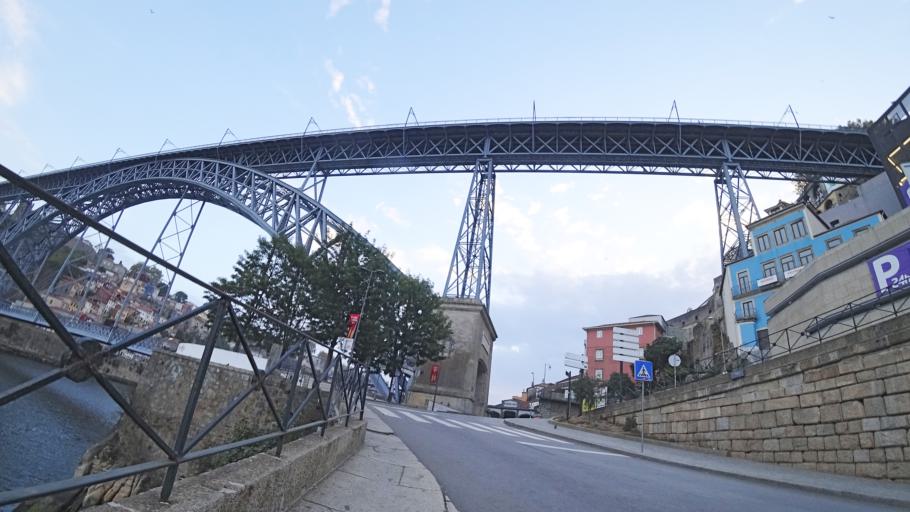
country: PT
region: Porto
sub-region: Vila Nova de Gaia
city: Vila Nova de Gaia
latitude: 41.1389
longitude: -8.6098
